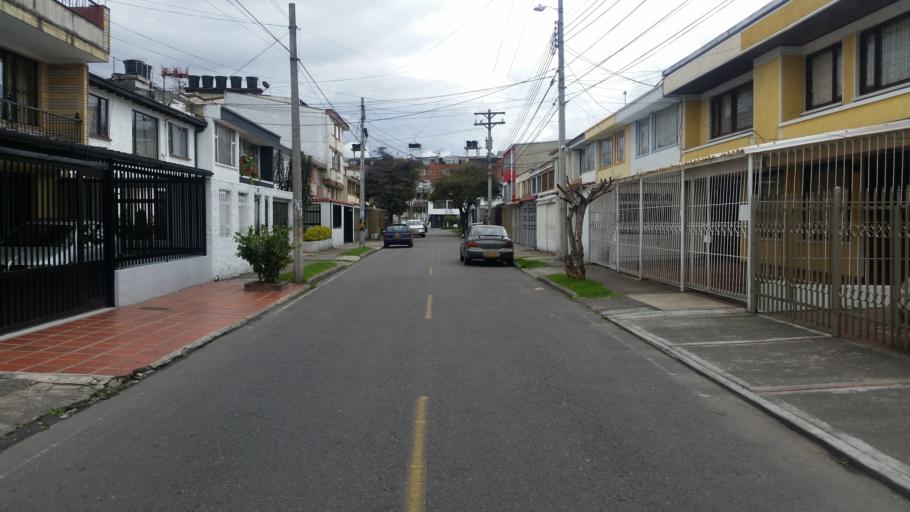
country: CO
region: Bogota D.C.
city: Bogota
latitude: 4.6701
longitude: -74.1114
